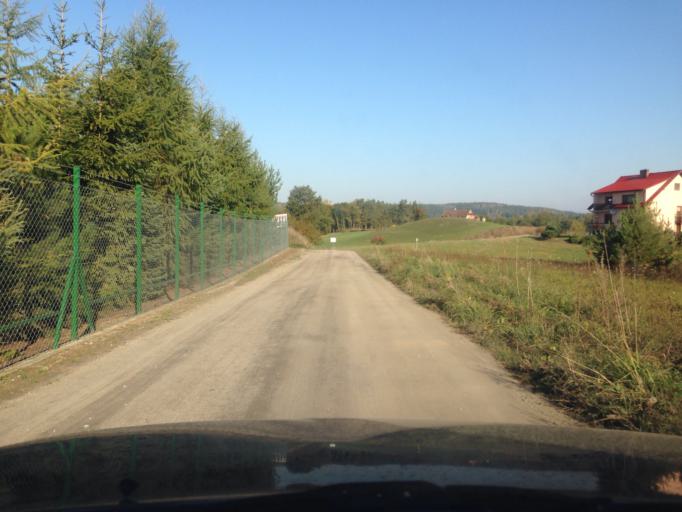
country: PL
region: Kujawsko-Pomorskie
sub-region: Powiat brodnicki
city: Gorzno
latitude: 53.2012
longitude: 19.6566
